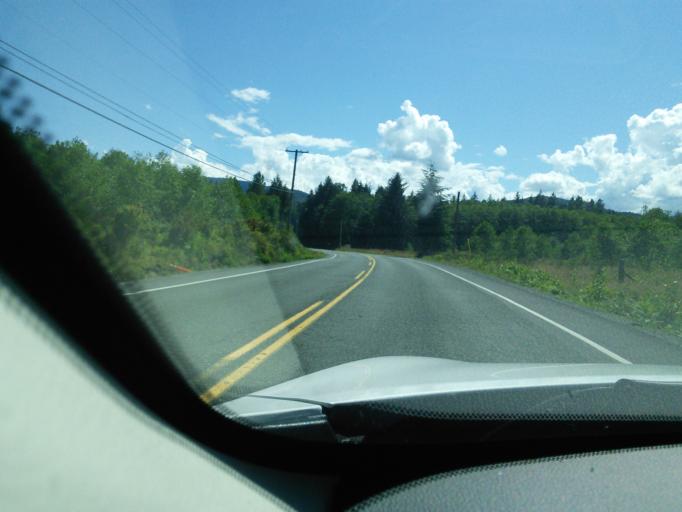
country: CA
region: British Columbia
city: Campbell River
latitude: 50.3273
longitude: -125.9217
